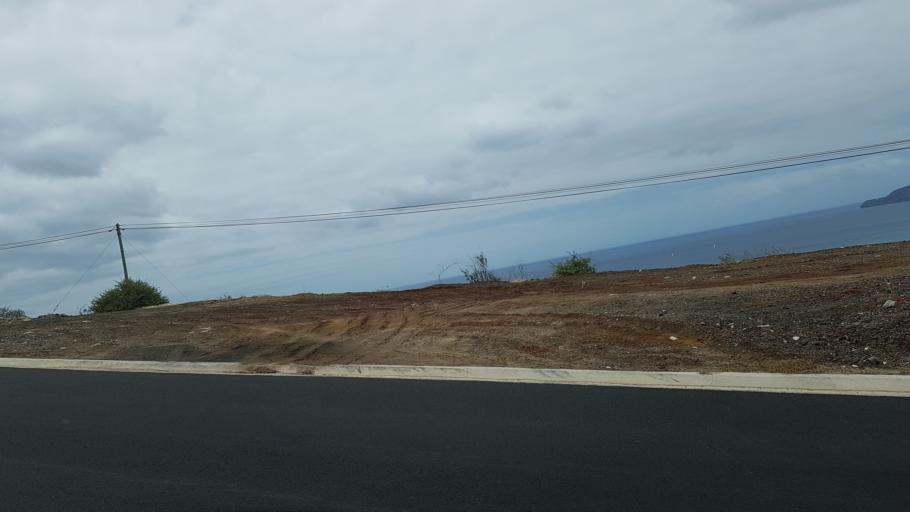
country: PT
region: Madeira
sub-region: Porto Santo
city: Vila de Porto Santo
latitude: 33.0706
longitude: -16.3232
